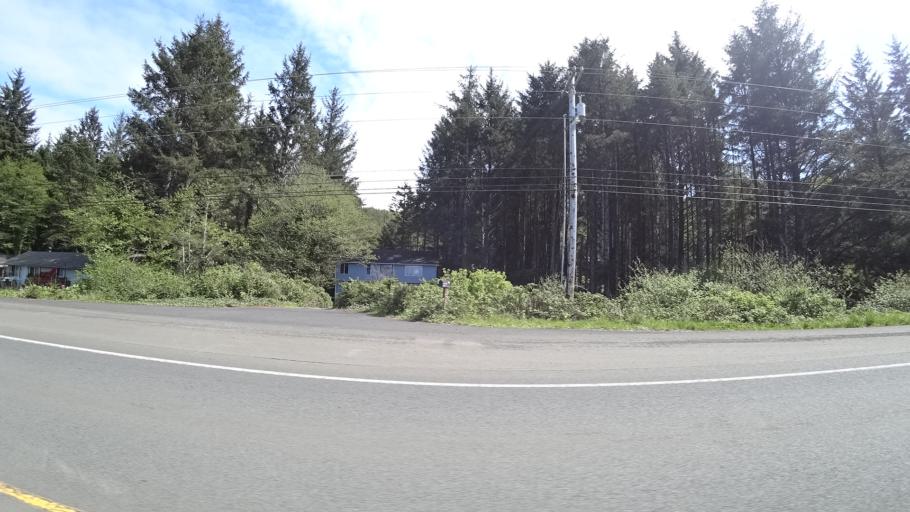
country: US
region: Oregon
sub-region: Lincoln County
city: Depoe Bay
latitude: 44.8294
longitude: -124.0584
